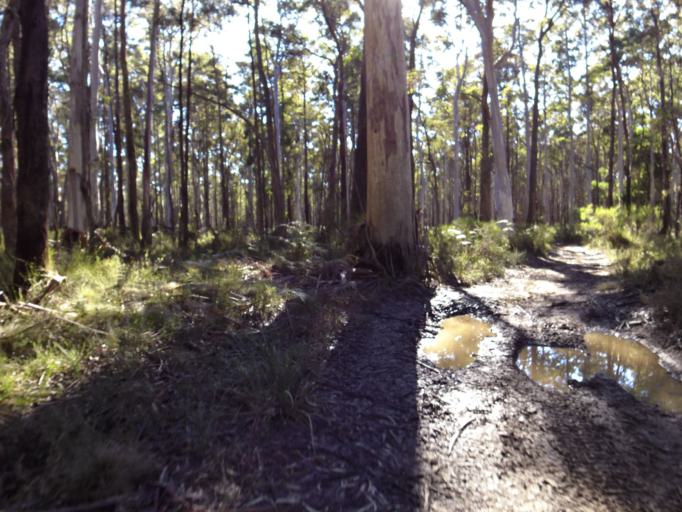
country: AU
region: Victoria
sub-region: Moorabool
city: Bacchus Marsh
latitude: -37.3920
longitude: 144.2872
